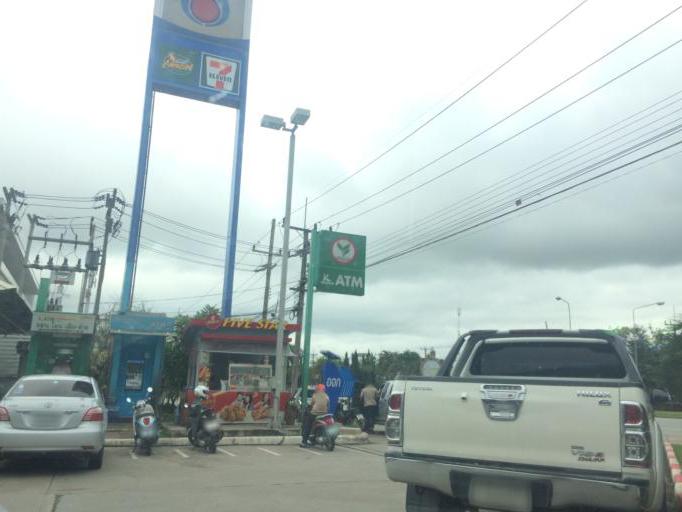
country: TH
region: Chiang Rai
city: Chiang Rai
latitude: 19.8755
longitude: 99.8294
